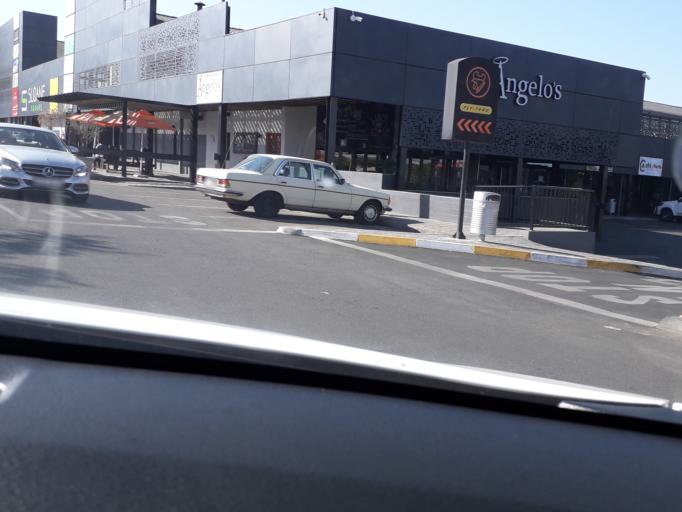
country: ZA
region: Gauteng
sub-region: City of Johannesburg Metropolitan Municipality
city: Diepsloot
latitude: -26.0431
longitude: 28.0150
